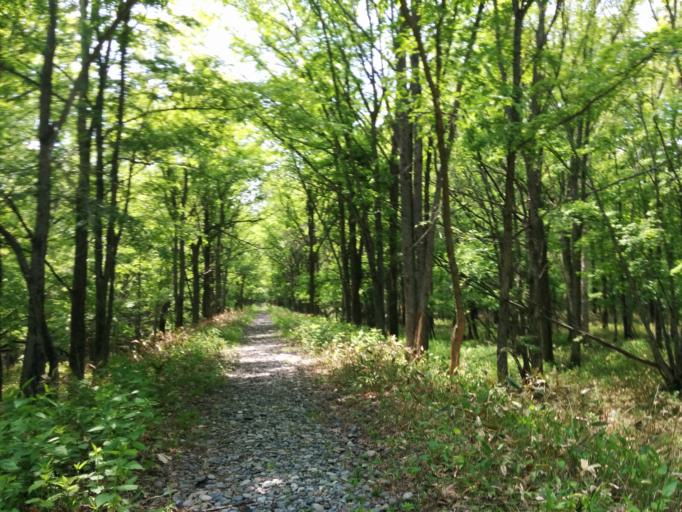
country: JP
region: Hokkaido
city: Otofuke
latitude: 43.4011
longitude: 143.1823
